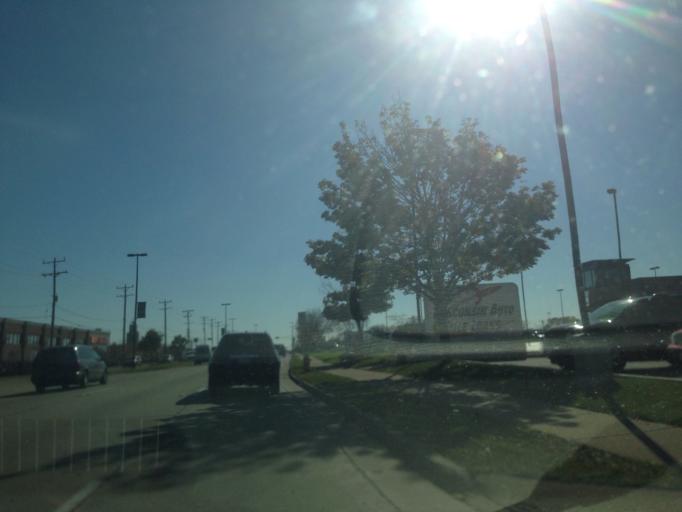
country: US
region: Wisconsin
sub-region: Milwaukee County
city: West Milwaukee
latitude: 43.0165
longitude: -87.9678
